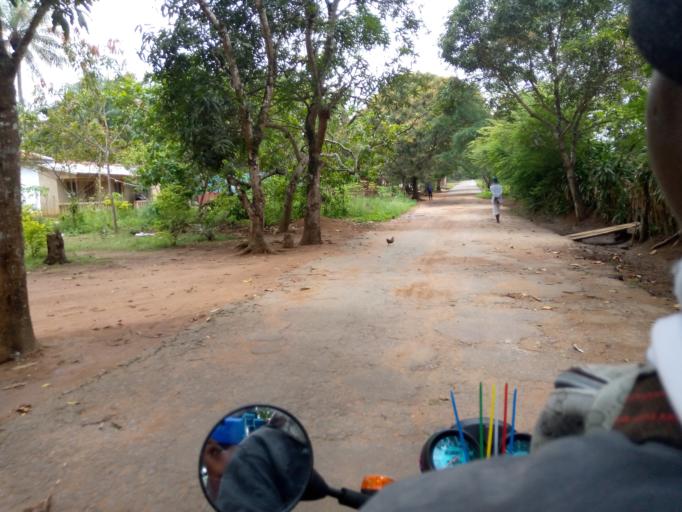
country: SL
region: Western Area
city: Waterloo
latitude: 8.3345
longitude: -12.9991
